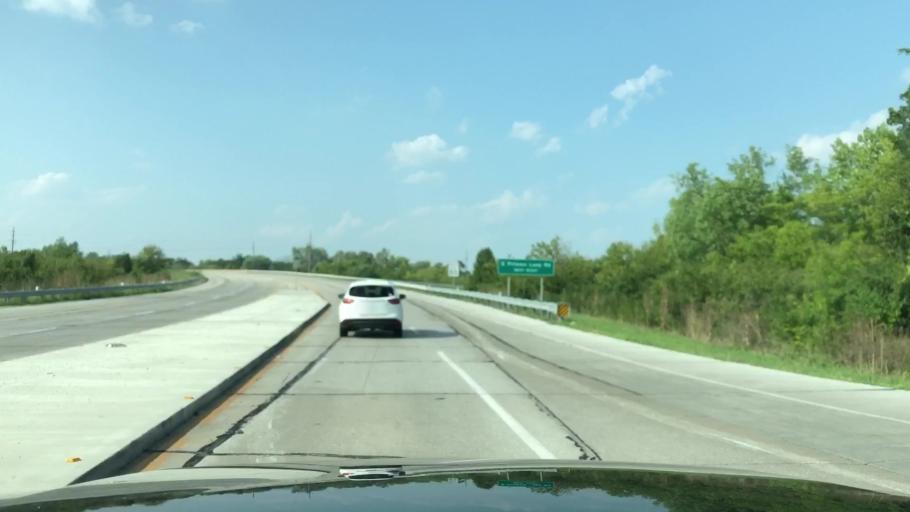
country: US
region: Missouri
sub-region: Saint Charles County
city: Lake Saint Louis
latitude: 38.8063
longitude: -90.8075
